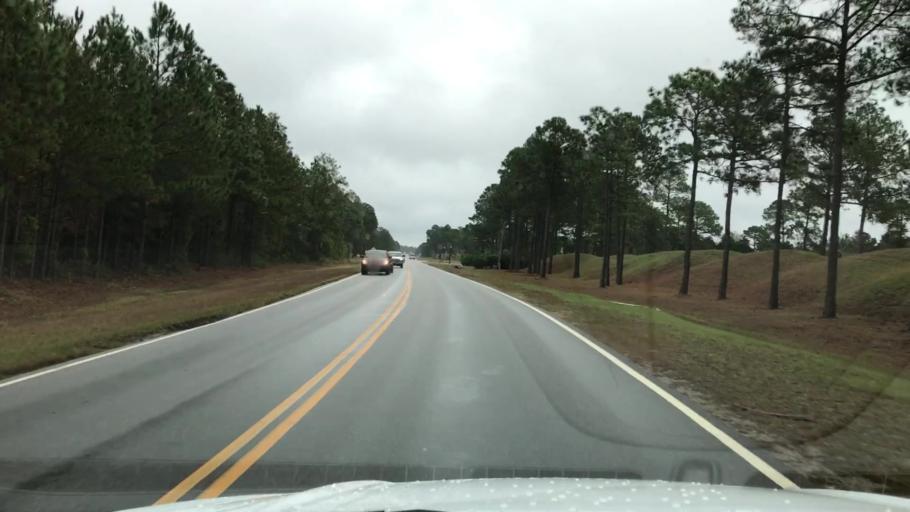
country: US
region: South Carolina
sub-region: Horry County
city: Forestbrook
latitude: 33.7568
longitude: -78.9120
